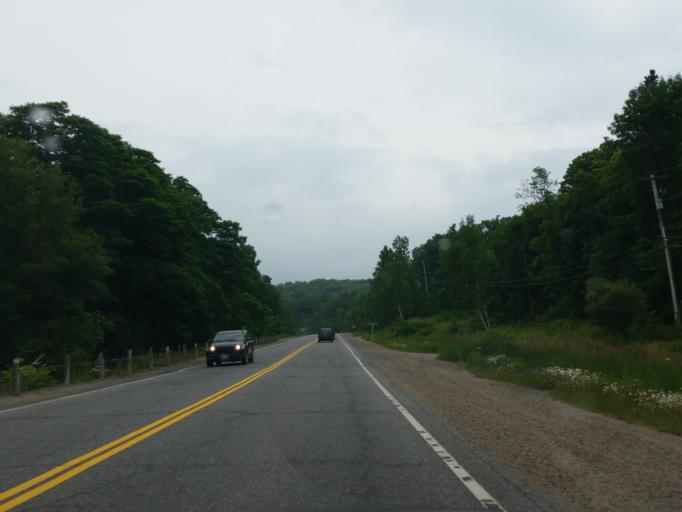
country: CA
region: Ontario
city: Huntsville
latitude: 45.3627
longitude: -79.1031
